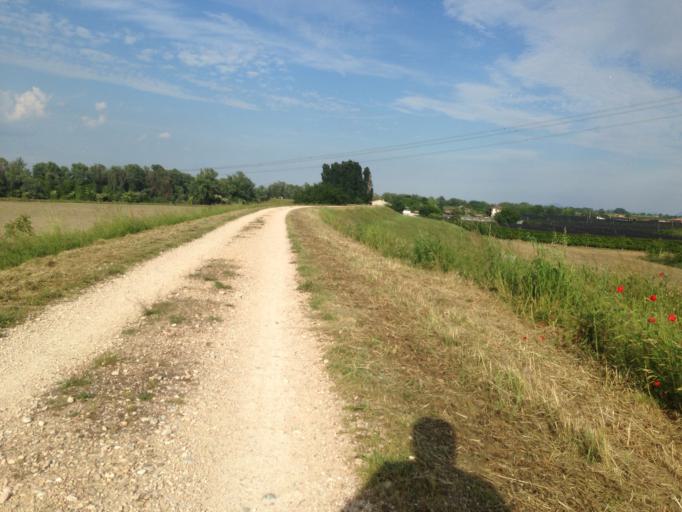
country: IT
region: Veneto
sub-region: Provincia di Verona
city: Belfiore
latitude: 45.3685
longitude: 11.1795
